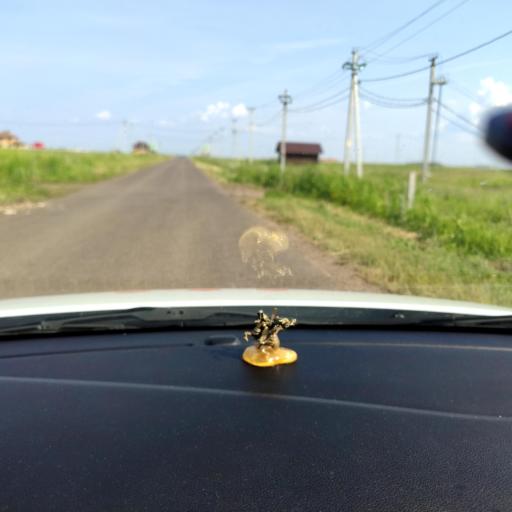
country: RU
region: Tatarstan
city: Laishevo
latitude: 55.4129
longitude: 49.3307
